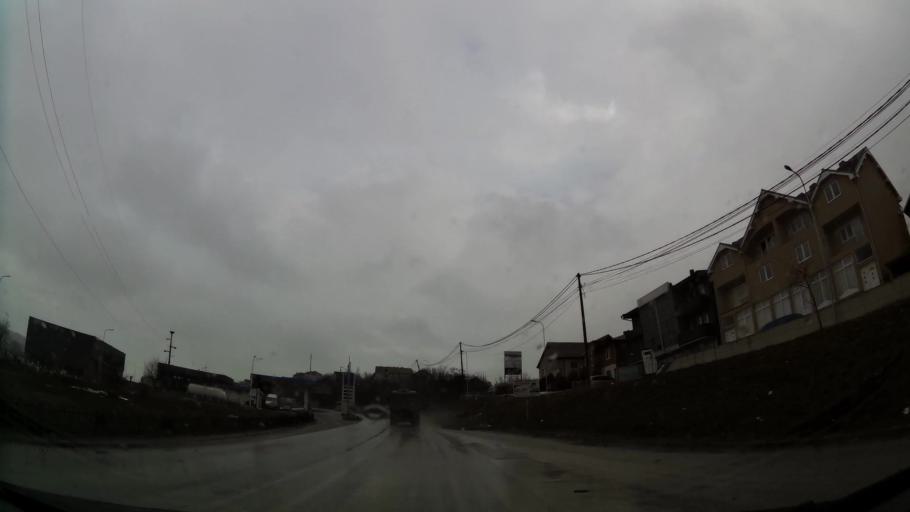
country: XK
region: Ferizaj
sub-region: Komuna e Kacanikut
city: Kacanik
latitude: 42.2311
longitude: 21.2543
